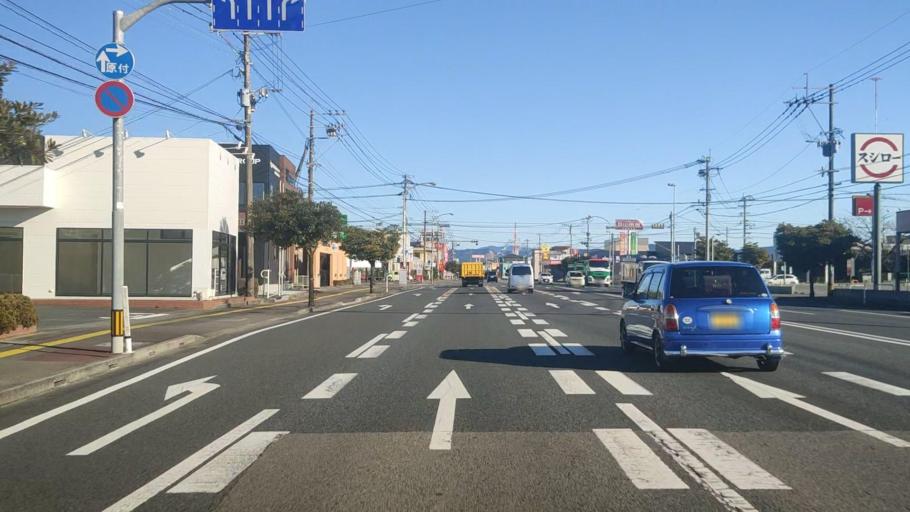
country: JP
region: Miyazaki
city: Nobeoka
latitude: 32.5510
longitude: 131.6777
